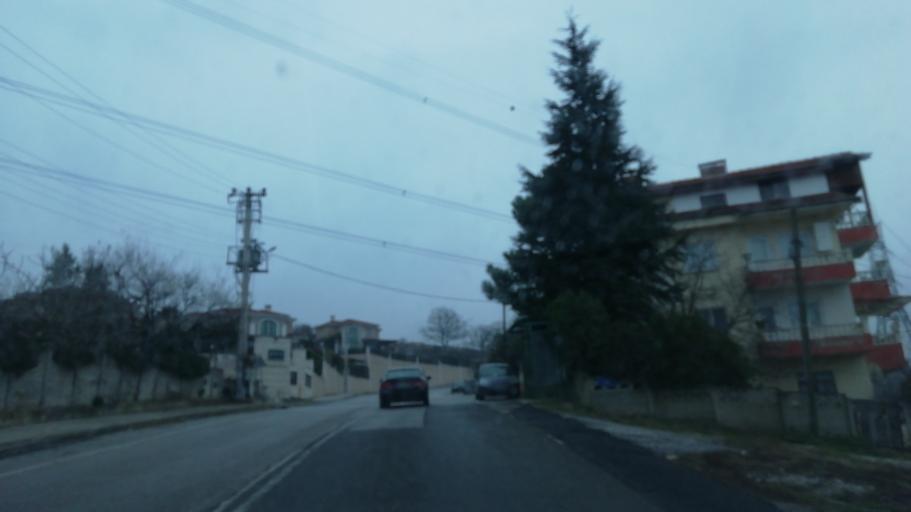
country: TR
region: Sakarya
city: Kazimpasa
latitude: 40.7430
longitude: 30.3158
